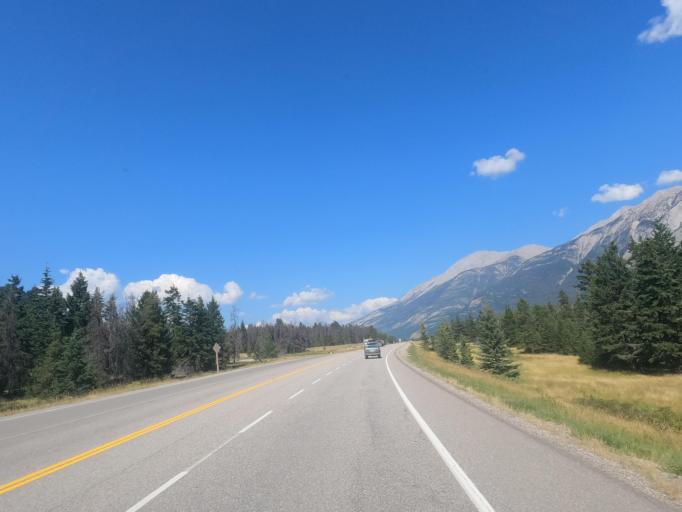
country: CA
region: Alberta
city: Jasper Park Lodge
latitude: 52.9388
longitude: -118.0393
